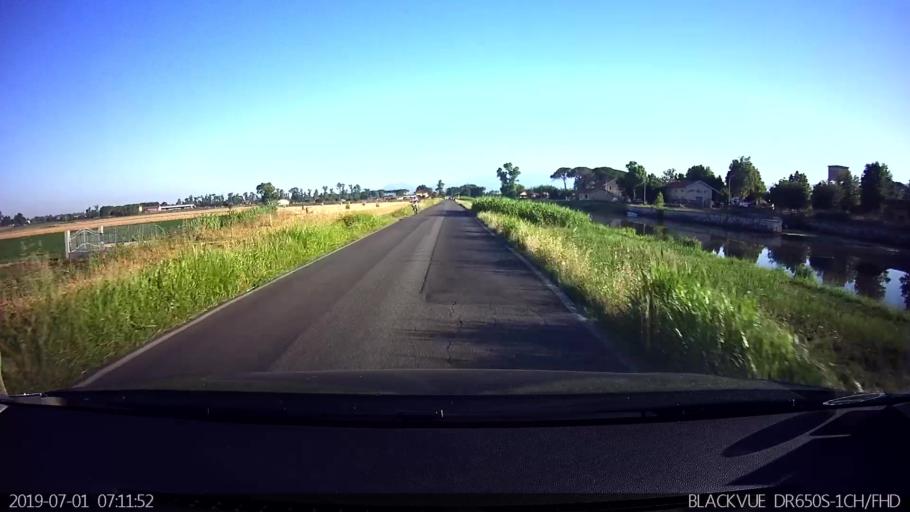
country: IT
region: Latium
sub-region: Provincia di Latina
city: Borgo Hermada
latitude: 41.3245
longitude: 13.1760
